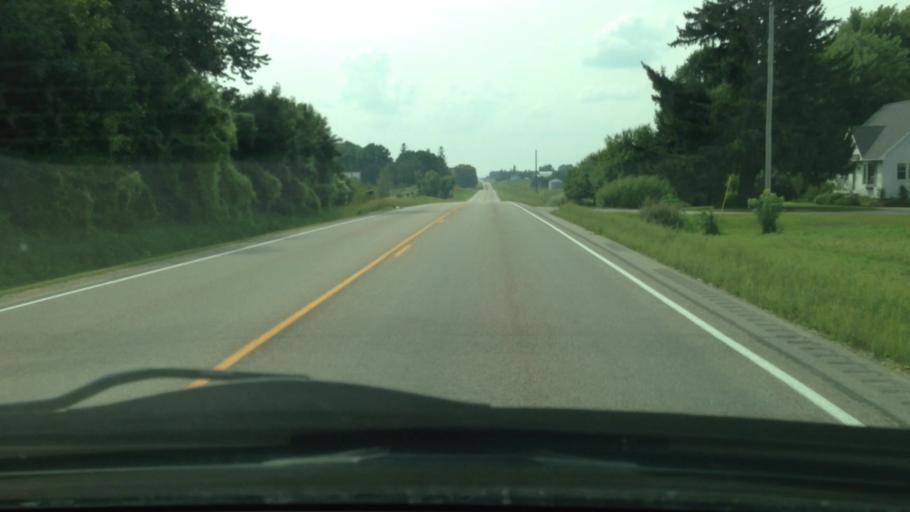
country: US
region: Minnesota
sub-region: Wabasha County
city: Plainview
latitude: 44.1651
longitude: -92.1889
